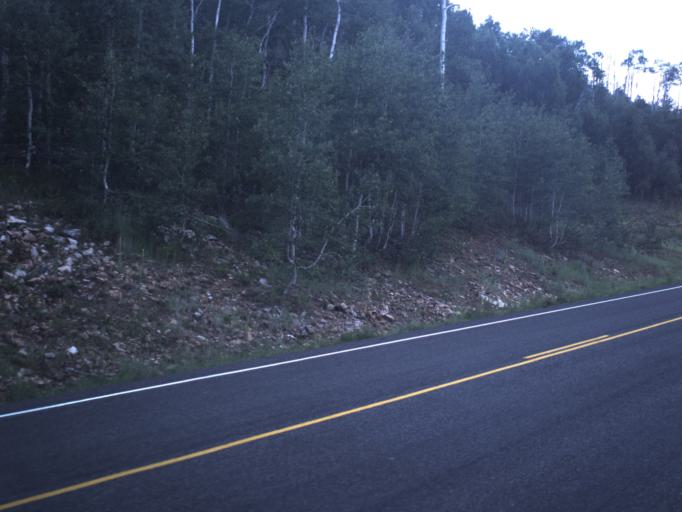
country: US
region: Utah
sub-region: Summit County
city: Francis
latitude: 40.5125
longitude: -111.0452
